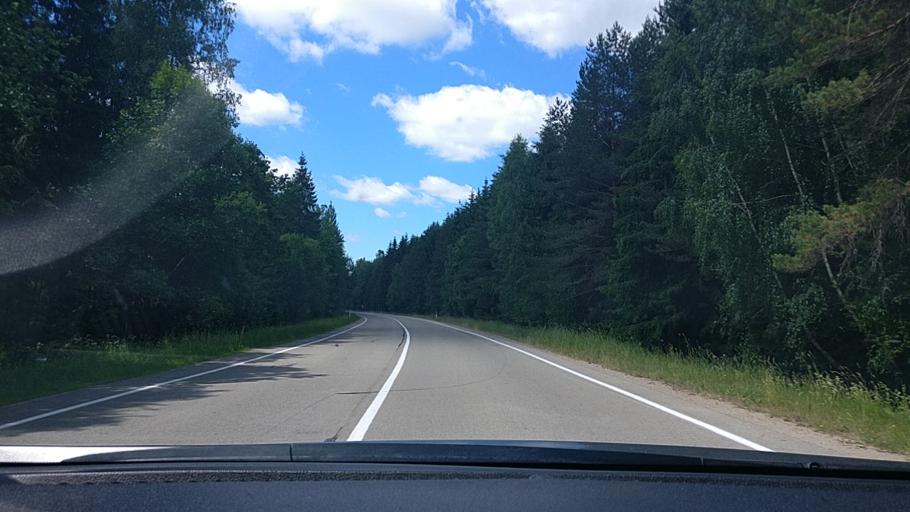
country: LT
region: Utenos apskritis
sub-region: Anyksciai
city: Anyksciai
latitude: 55.6542
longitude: 25.0759
